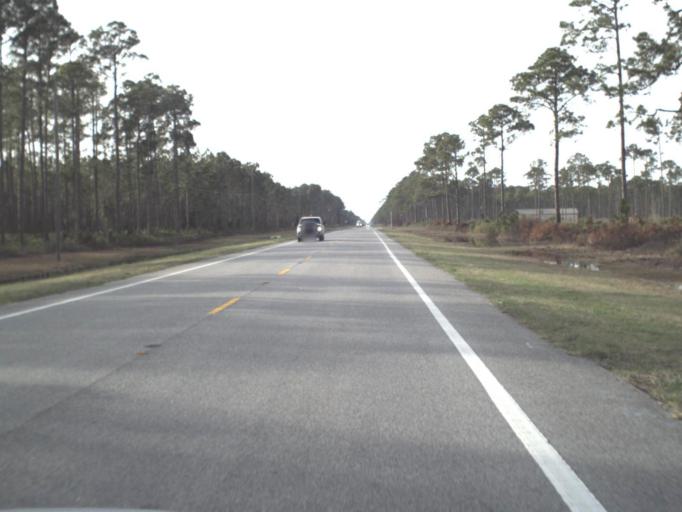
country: US
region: Florida
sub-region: Bay County
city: Mexico Beach
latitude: 29.9963
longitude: -85.4947
